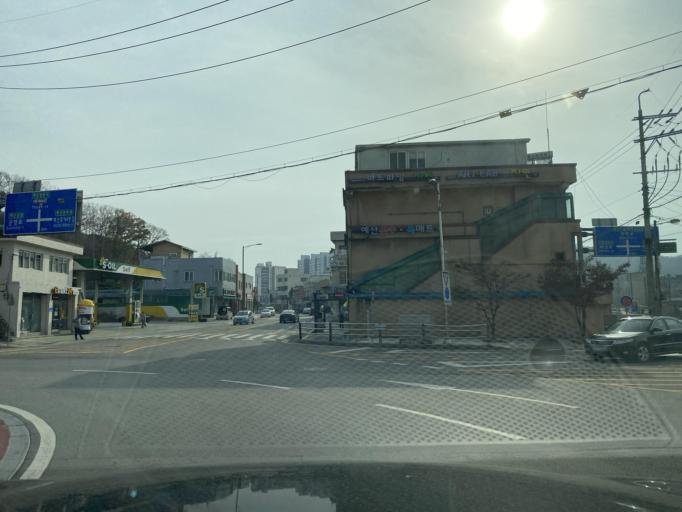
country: KR
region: Chungcheongnam-do
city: Yesan
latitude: 36.6815
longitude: 126.8328
